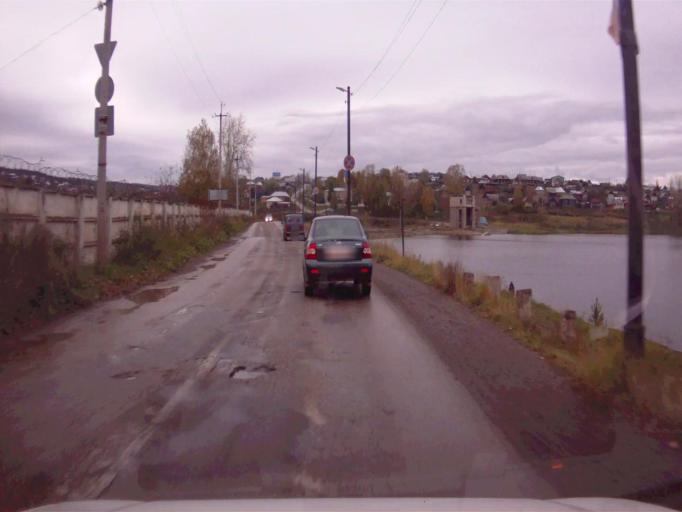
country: RU
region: Chelyabinsk
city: Nyazepetrovsk
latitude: 56.0545
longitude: 59.5934
